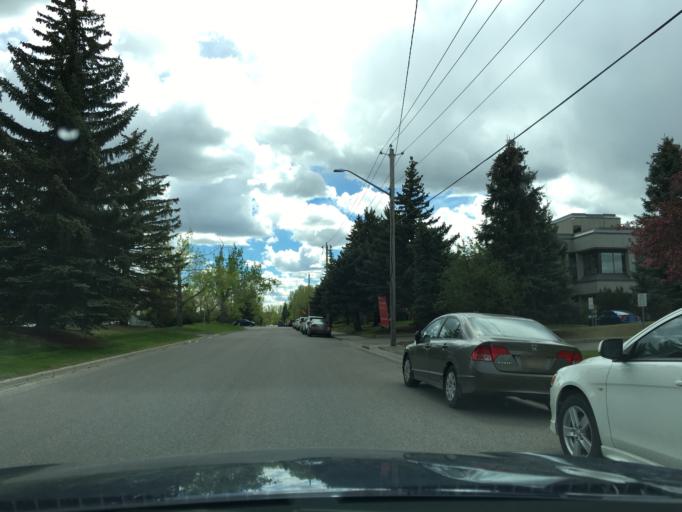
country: CA
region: Alberta
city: Calgary
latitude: 50.9110
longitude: -114.0641
